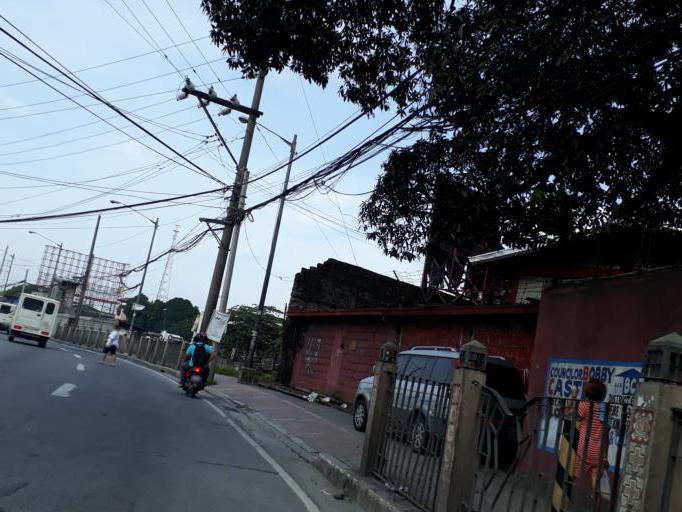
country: PH
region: Calabarzon
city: Del Monte
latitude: 14.6648
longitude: 121.0036
